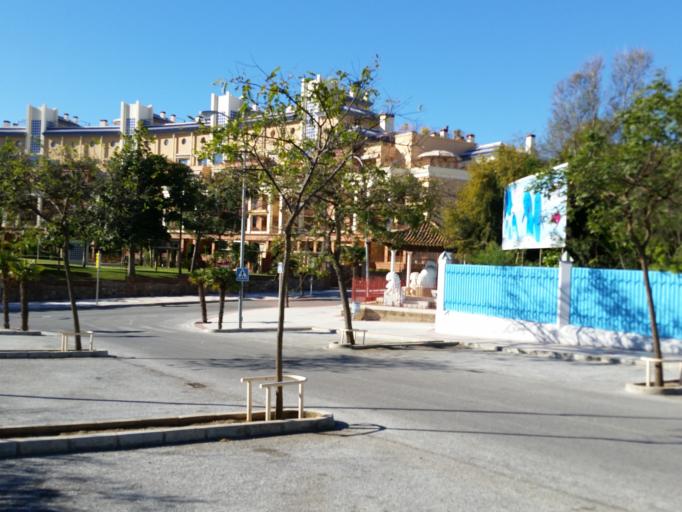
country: ES
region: Andalusia
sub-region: Provincia de Malaga
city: Benalmadena
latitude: 36.5922
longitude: -4.5311
